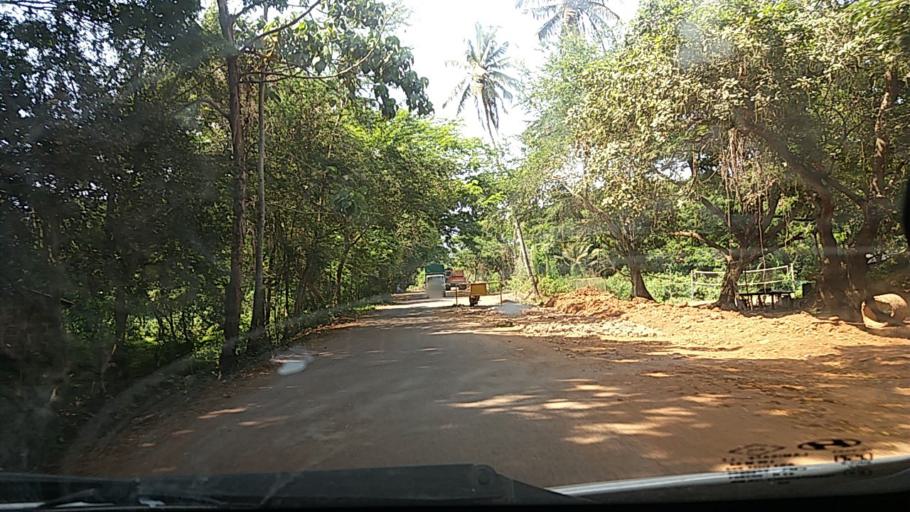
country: IN
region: Goa
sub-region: South Goa
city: Madgaon
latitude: 15.2780
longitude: 73.9530
